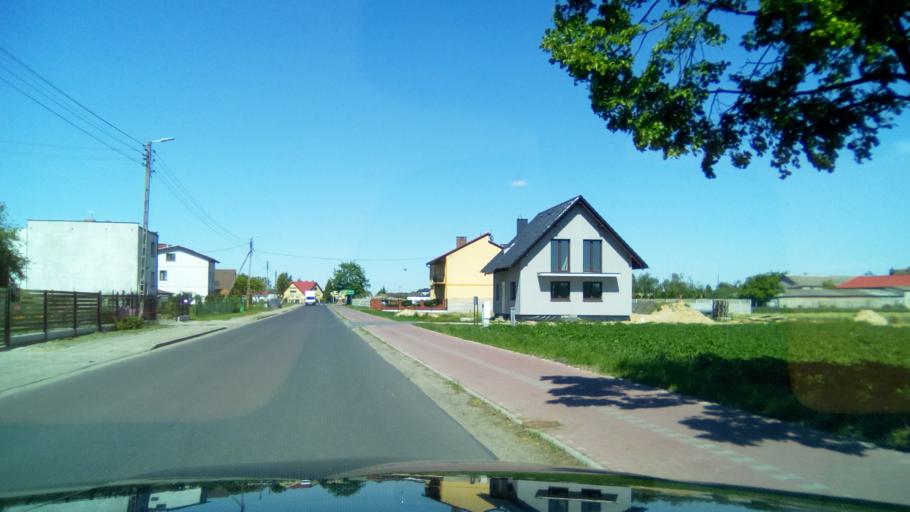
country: PL
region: Greater Poland Voivodeship
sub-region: Powiat gnieznienski
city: Niechanowo
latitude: 52.4688
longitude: 17.6832
